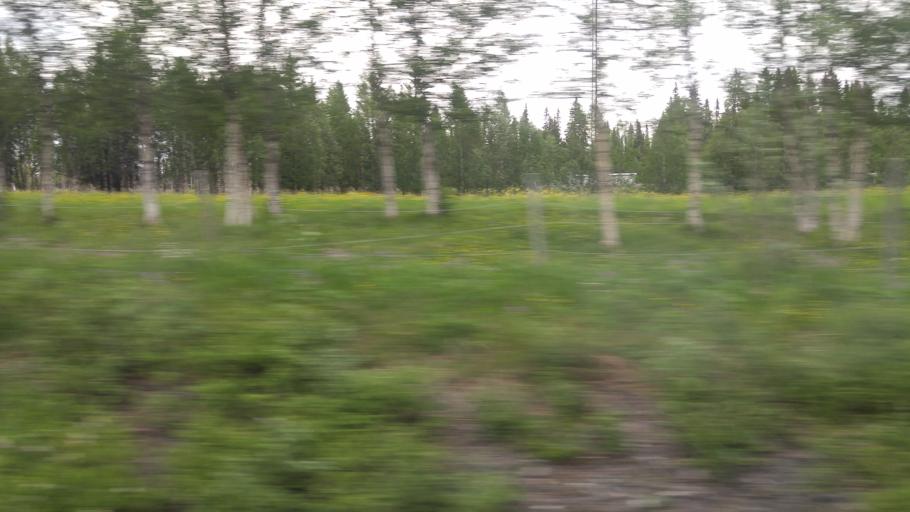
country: SE
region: Jaemtland
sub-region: Are Kommun
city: Are
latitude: 63.3575
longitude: 12.6094
